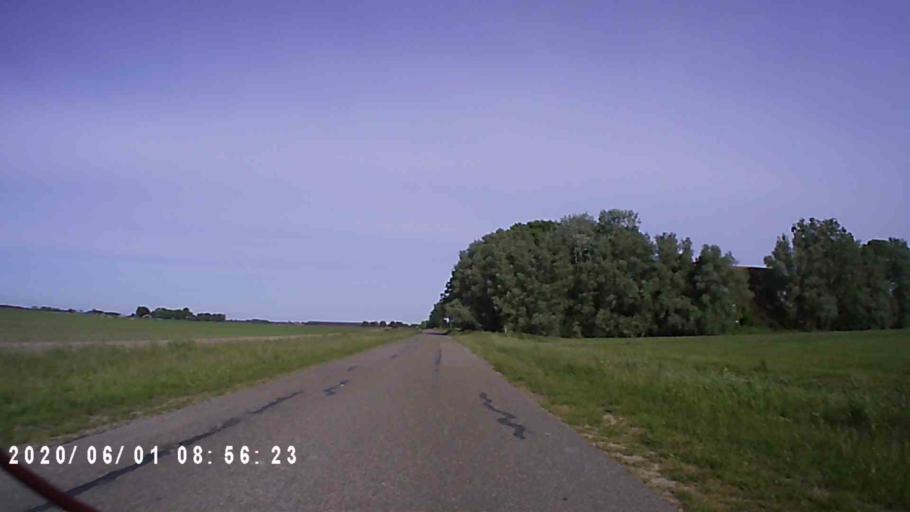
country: NL
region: Friesland
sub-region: Gemeente Leeuwarderadeel
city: Britsum
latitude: 53.2794
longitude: 5.8193
